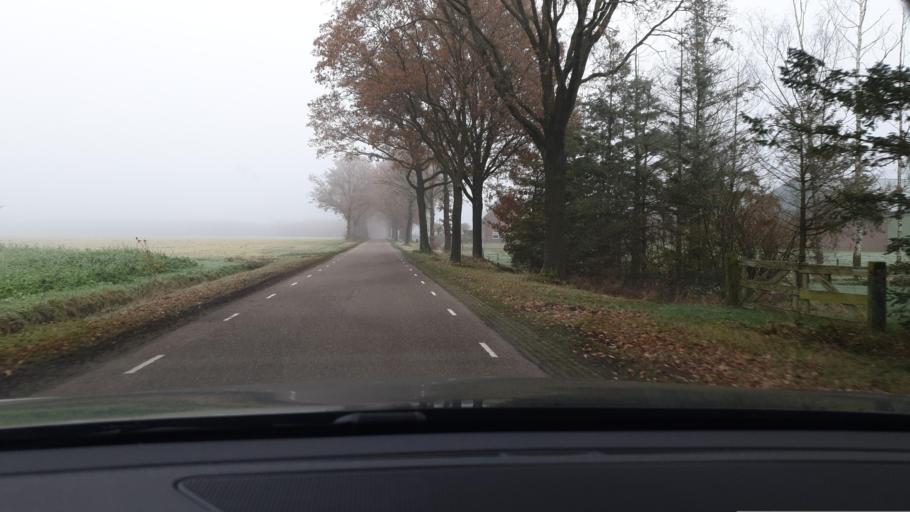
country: NL
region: North Brabant
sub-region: Gemeente Bladel en Netersel
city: Bladel
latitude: 51.3936
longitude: 5.1926
